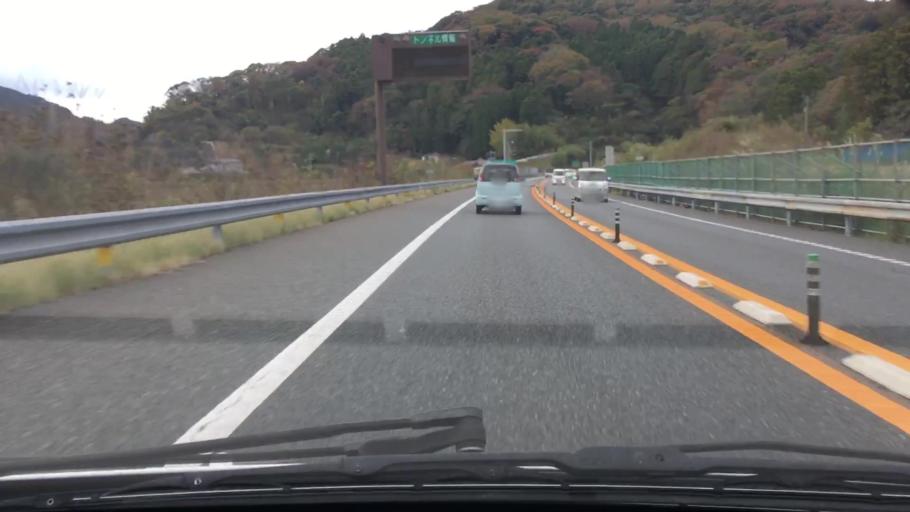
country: JP
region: Chiba
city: Futtsu
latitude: 35.2069
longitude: 139.8806
